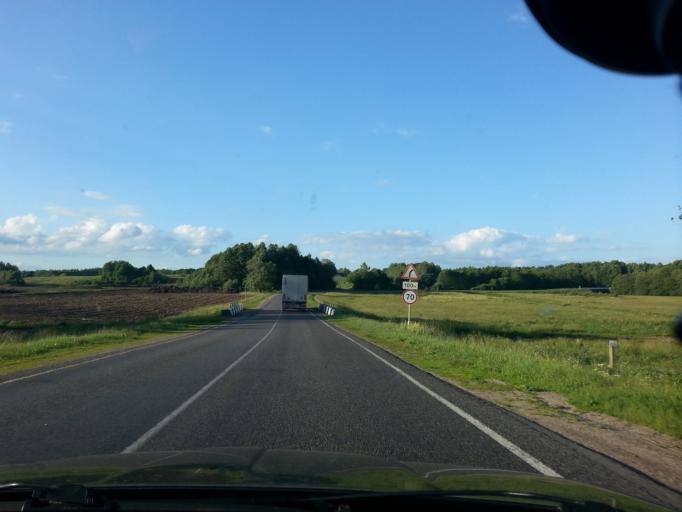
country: BY
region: Minsk
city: Svir
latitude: 54.8596
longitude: 26.3197
